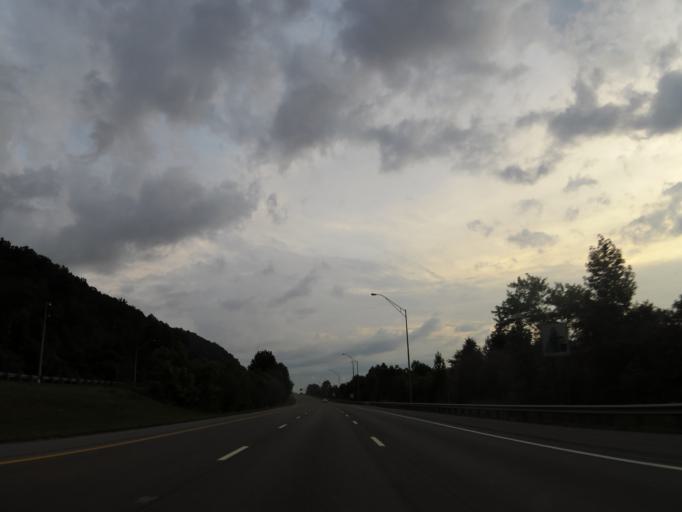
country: US
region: Tennessee
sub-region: Knox County
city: Knoxville
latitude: 36.0297
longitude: -83.8972
